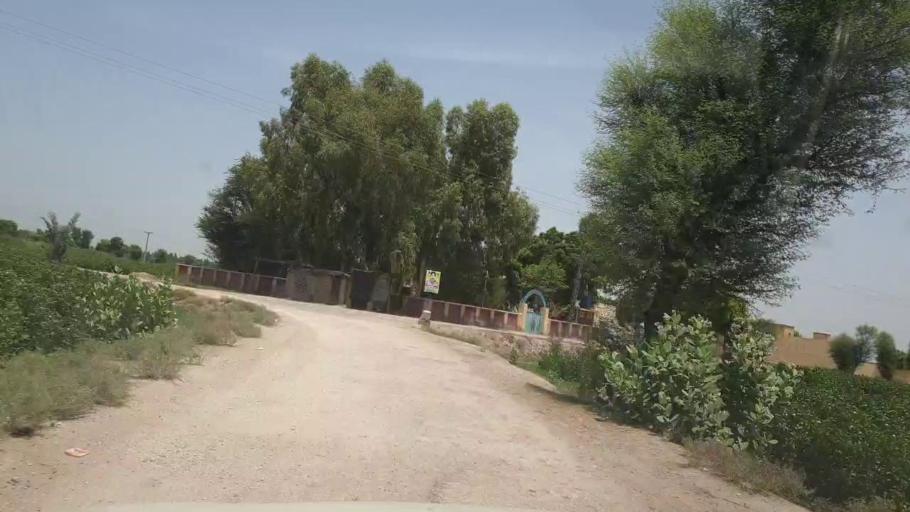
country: PK
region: Sindh
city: Bozdar
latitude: 27.1605
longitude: 68.6157
